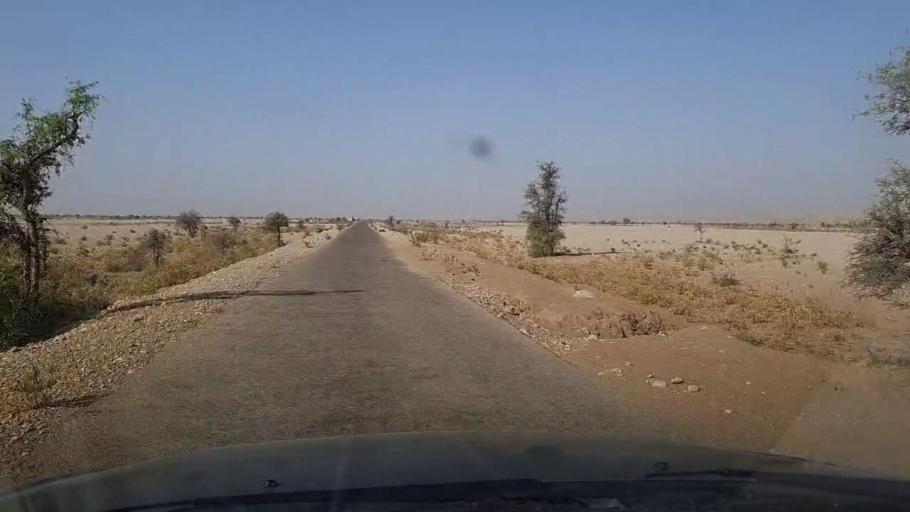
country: PK
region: Sindh
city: Sann
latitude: 25.9072
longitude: 68.0053
